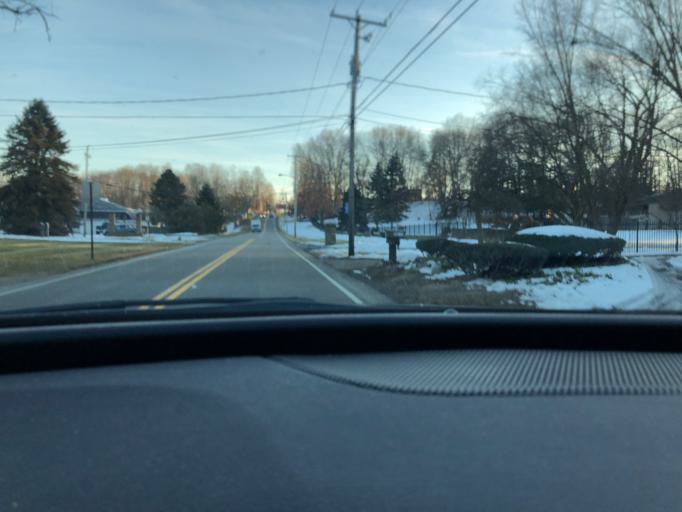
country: US
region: Ohio
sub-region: Stark County
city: Perry Heights
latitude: 40.8095
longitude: -81.4655
